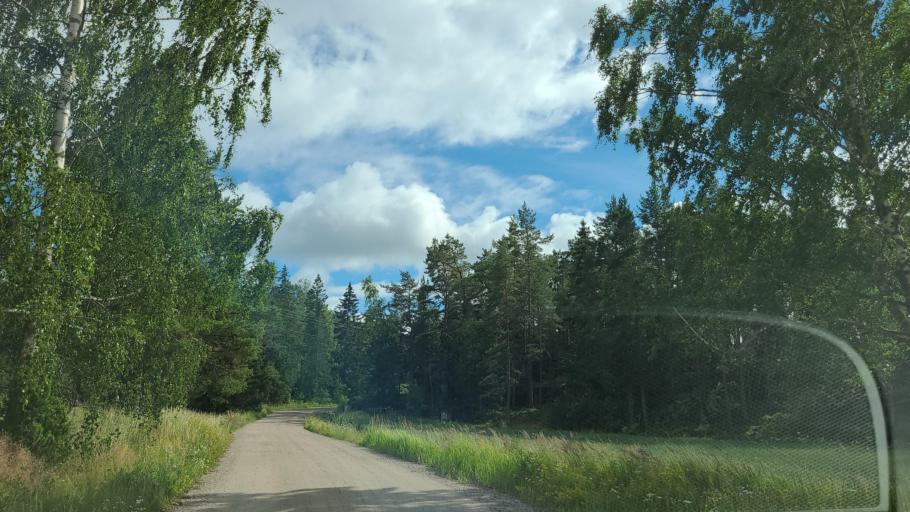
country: FI
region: Varsinais-Suomi
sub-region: Aboland-Turunmaa
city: Nagu
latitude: 60.1977
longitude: 21.7759
